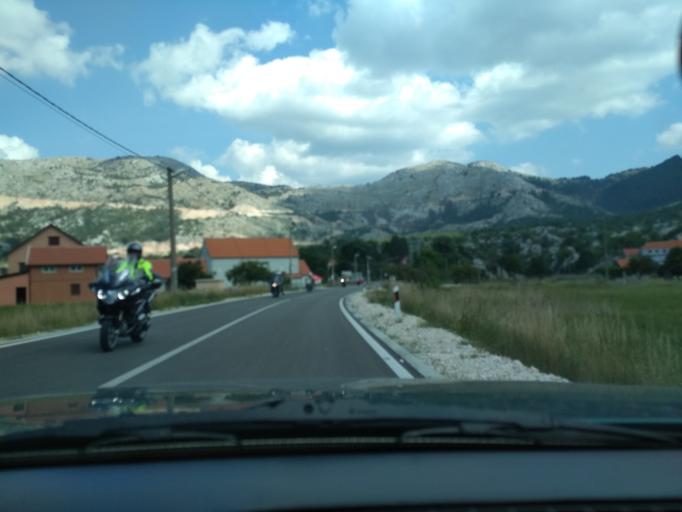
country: ME
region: Kotor
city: Kotor
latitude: 42.4298
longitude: 18.8257
